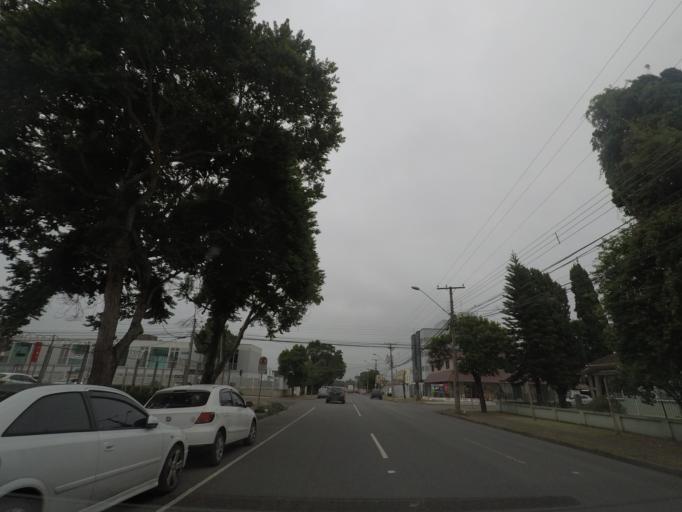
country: BR
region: Parana
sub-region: Curitiba
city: Curitiba
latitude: -25.4789
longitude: -49.2499
